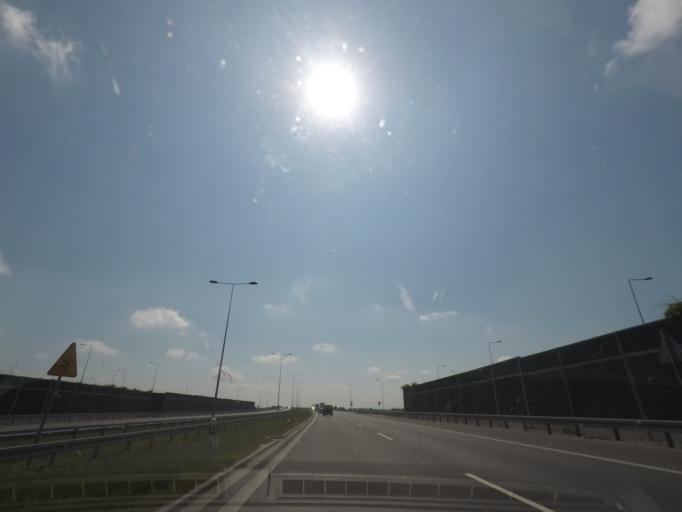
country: PL
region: Kujawsko-Pomorskie
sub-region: Powiat wloclawski
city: Chocen
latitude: 52.5675
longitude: 19.0129
